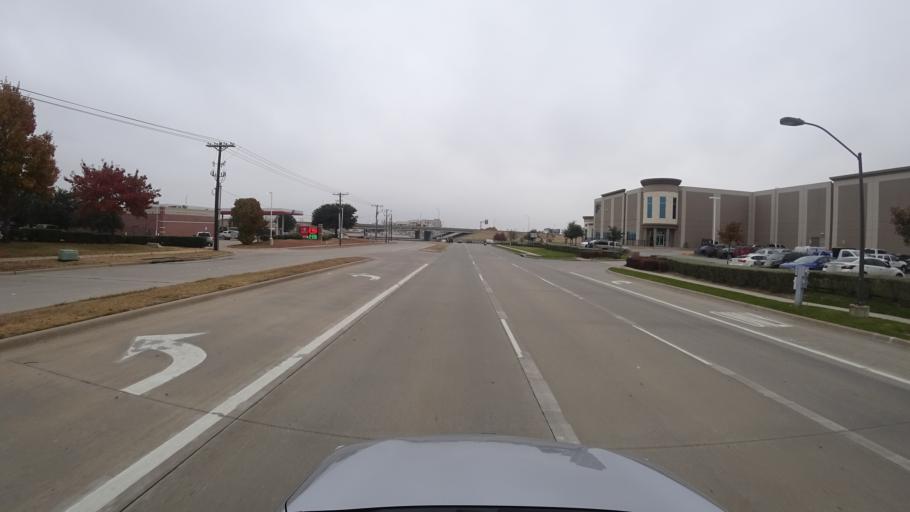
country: US
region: Texas
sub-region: Denton County
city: The Colony
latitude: 33.0623
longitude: -96.9017
